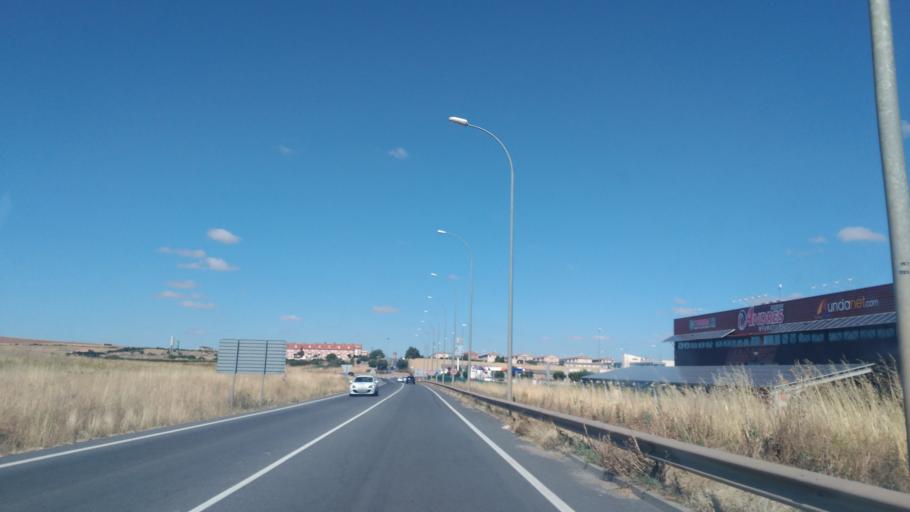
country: ES
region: Castille and Leon
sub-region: Provincia de Salamanca
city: Doninos de Salamanca
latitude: 40.9590
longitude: -5.7246
